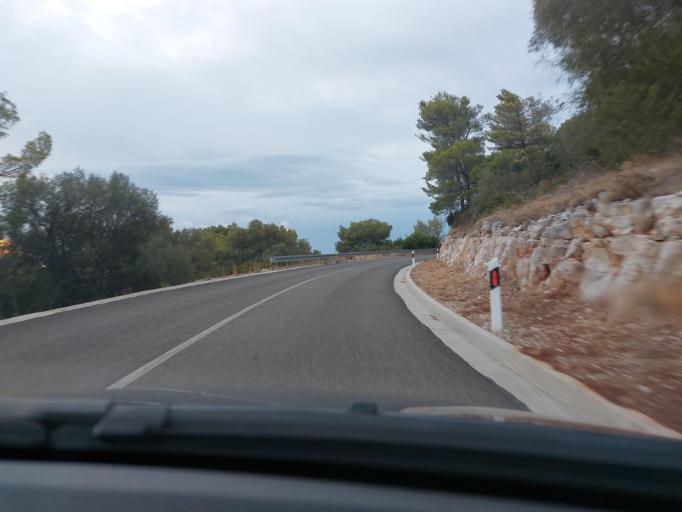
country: HR
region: Dubrovacko-Neretvanska
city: Smokvica
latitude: 42.7644
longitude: 16.8509
